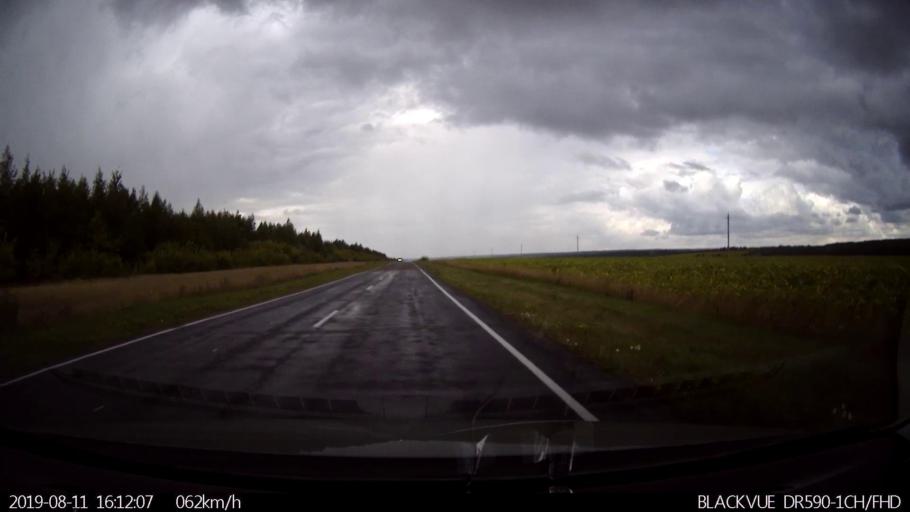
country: RU
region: Ulyanovsk
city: Ignatovka
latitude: 54.0088
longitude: 47.6415
